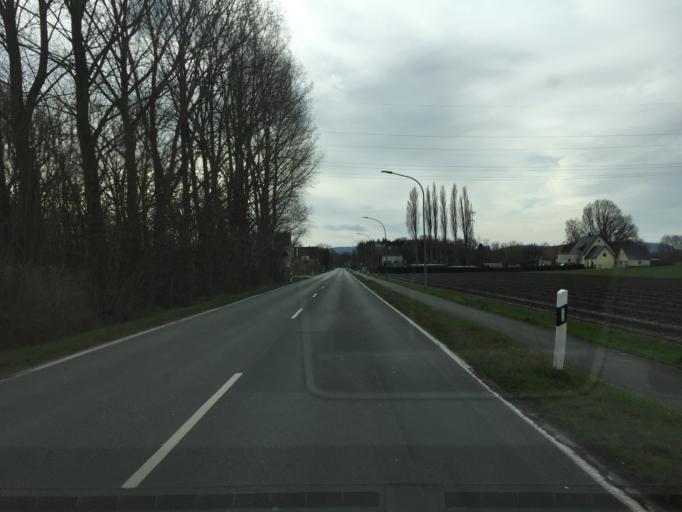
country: DE
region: North Rhine-Westphalia
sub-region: Regierungsbezirk Detmold
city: Lage
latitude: 51.9788
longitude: 8.7982
